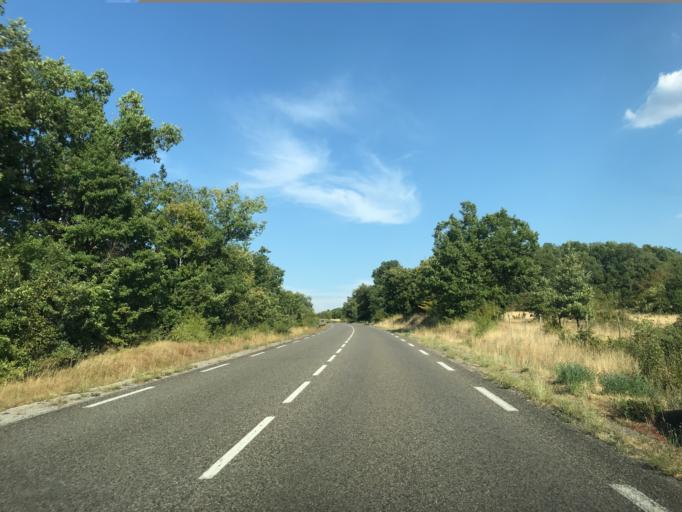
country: FR
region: Midi-Pyrenees
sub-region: Departement du Lot
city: Gramat
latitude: 44.6784
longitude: 1.6348
